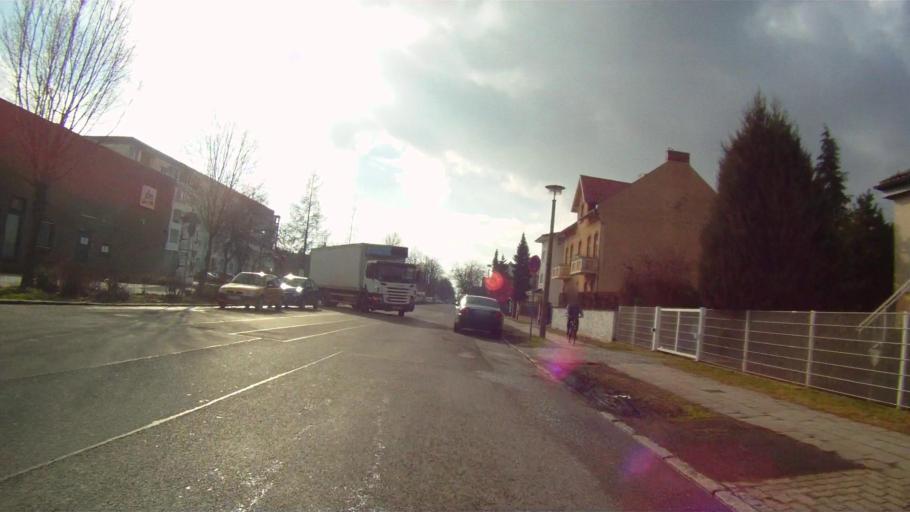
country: DE
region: Berlin
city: Biesdorf
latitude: 52.5249
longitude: 13.5569
